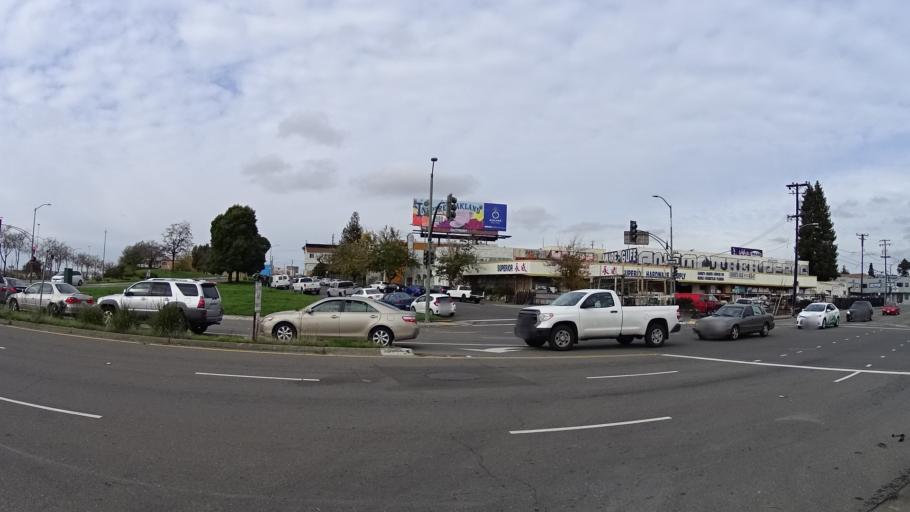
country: US
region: California
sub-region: Alameda County
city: Alameda
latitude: 37.7883
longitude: -122.2468
